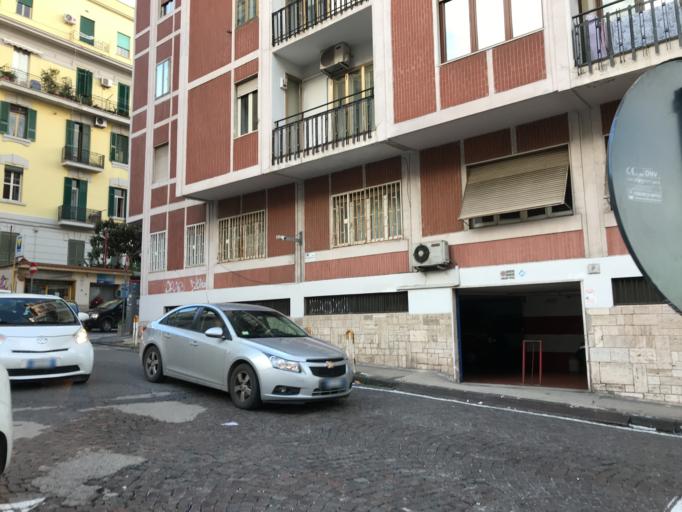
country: IT
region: Campania
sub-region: Provincia di Napoli
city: Napoli
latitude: 40.8537
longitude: 14.2331
